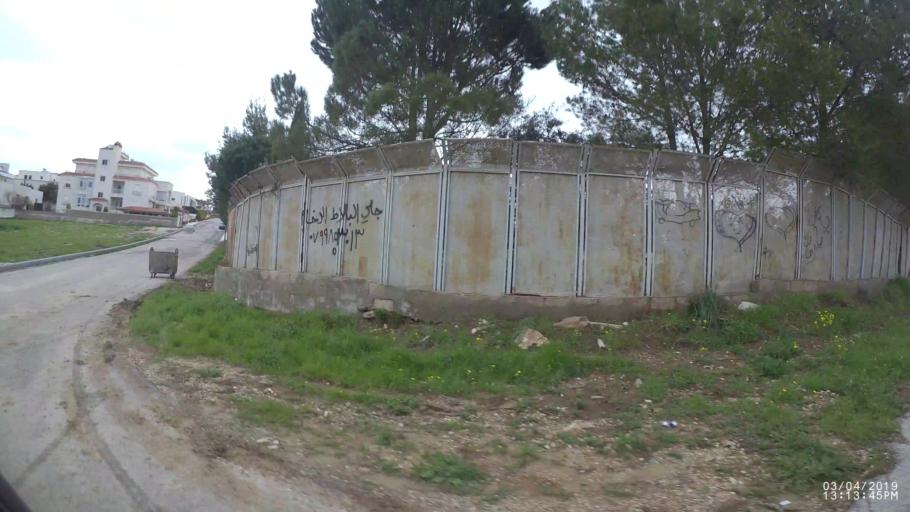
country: JO
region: Amman
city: Wadi as Sir
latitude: 31.9601
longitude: 35.8230
